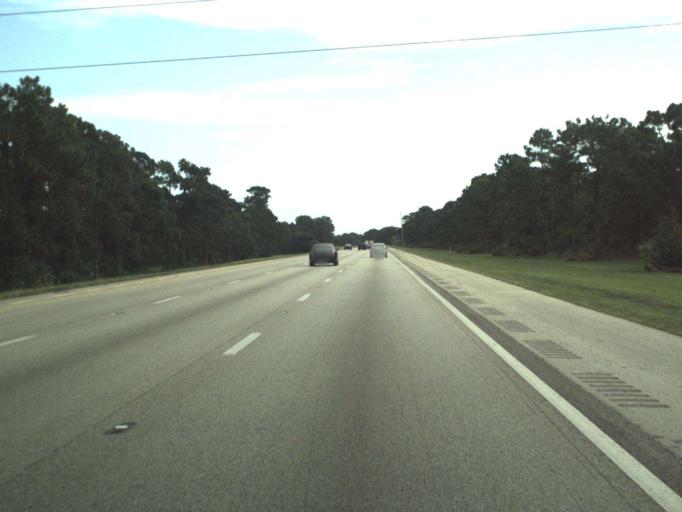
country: US
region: Florida
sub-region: Saint Lucie County
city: River Park
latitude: 27.3205
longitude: -80.4133
